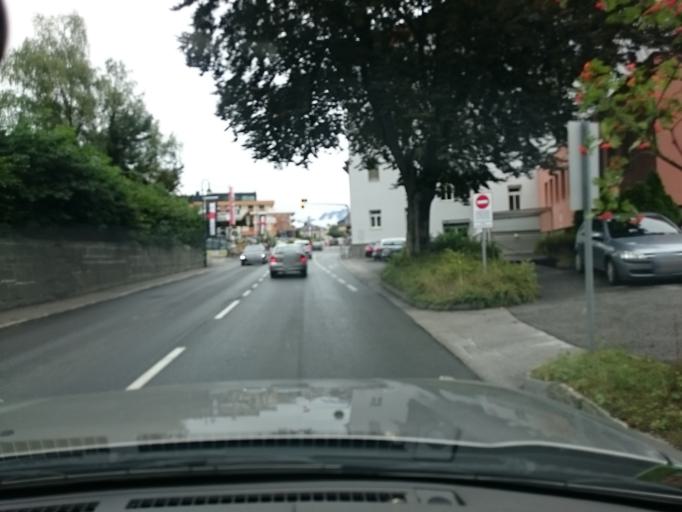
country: AT
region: Salzburg
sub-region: Politischer Bezirk Zell am See
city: Zell am See
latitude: 47.3202
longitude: 12.7952
